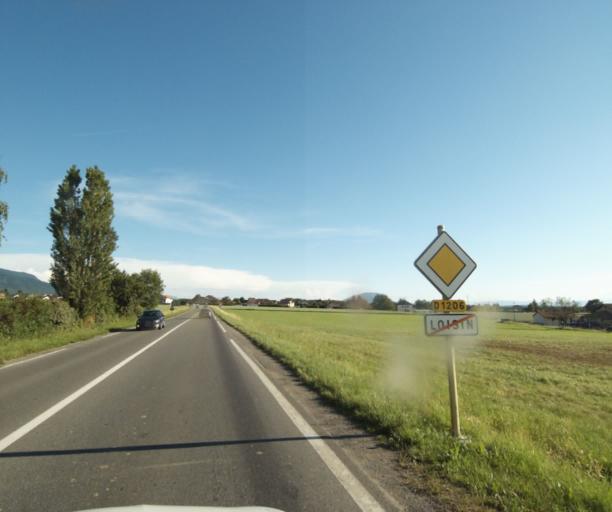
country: FR
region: Rhone-Alpes
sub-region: Departement de la Haute-Savoie
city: Loisin
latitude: 46.2874
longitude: 6.3094
